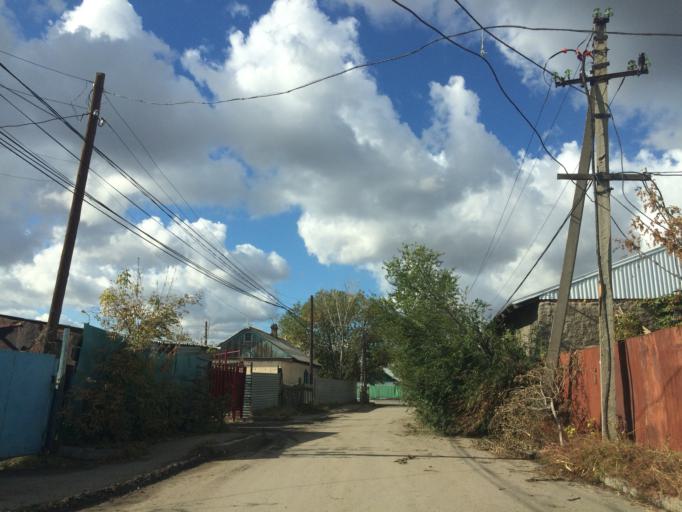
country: KZ
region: Astana Qalasy
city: Astana
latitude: 51.1914
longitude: 71.3883
